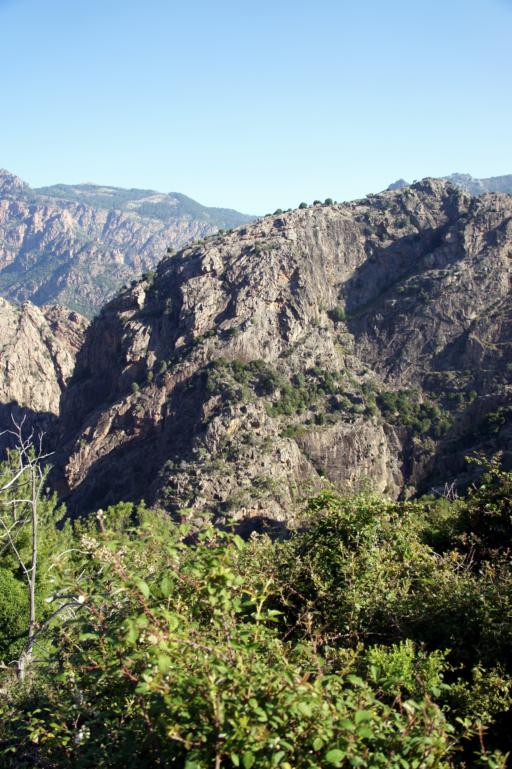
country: FR
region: Corsica
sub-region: Departement de la Corse-du-Sud
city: Cargese
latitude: 42.2418
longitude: 8.7788
